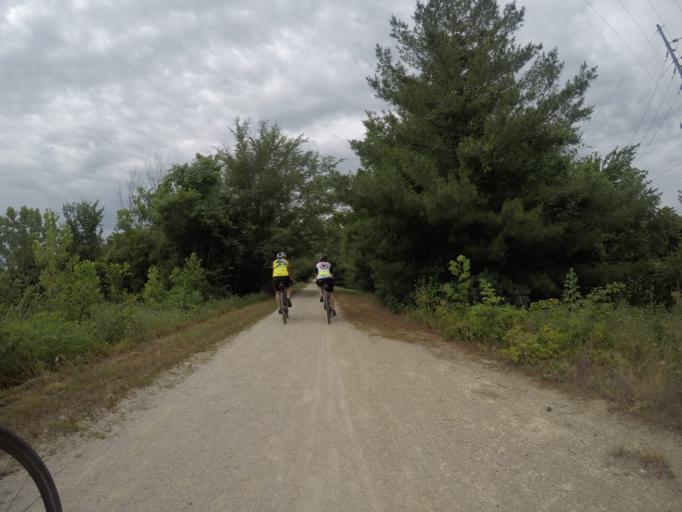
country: US
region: Kansas
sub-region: Anderson County
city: Garnett
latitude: 38.2701
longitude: -95.2435
